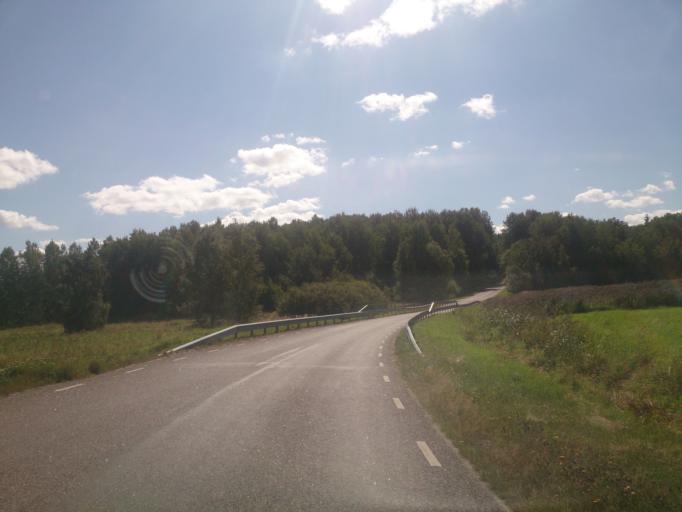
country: SE
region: OEstergoetland
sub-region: Atvidabergs Kommun
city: Atvidaberg
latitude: 58.2848
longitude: 16.0347
